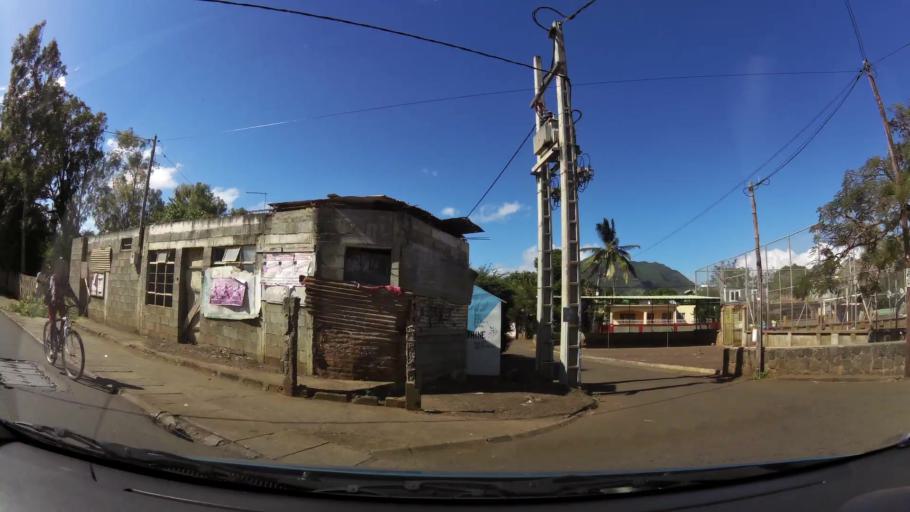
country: MU
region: Black River
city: Cascavelle
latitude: -20.2500
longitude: 57.4200
